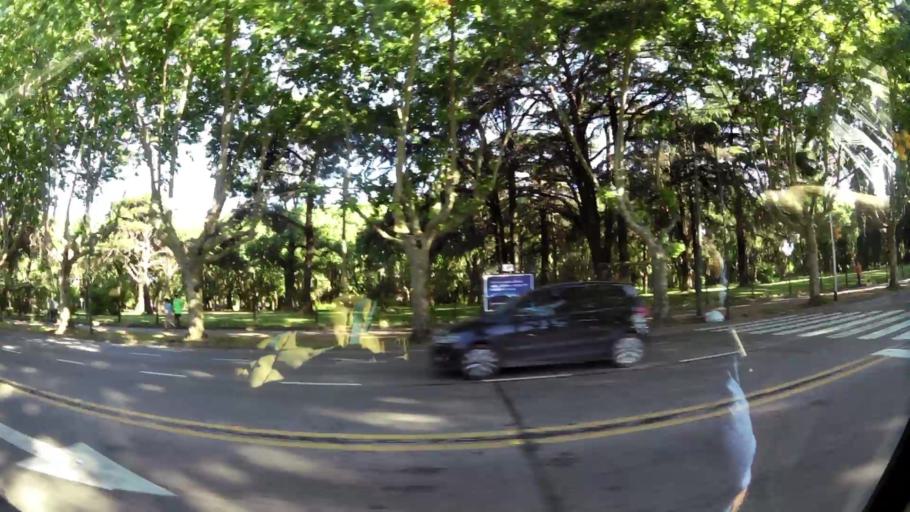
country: AR
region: Buenos Aires
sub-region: Partido de San Isidro
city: San Isidro
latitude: -34.4760
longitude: -58.5158
